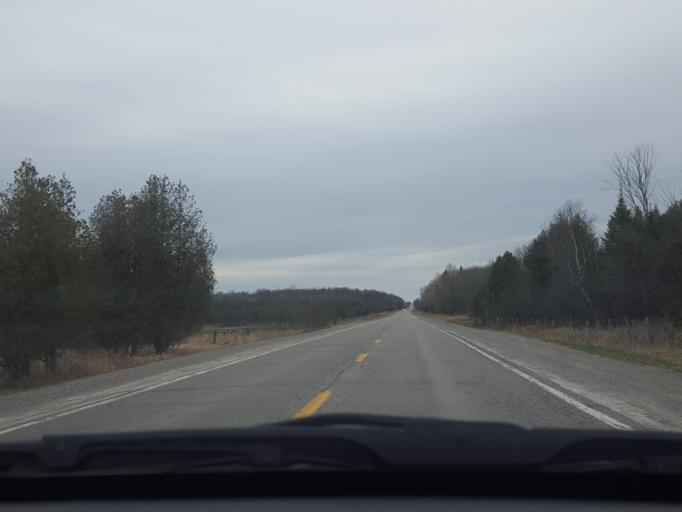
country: CA
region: Ontario
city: Uxbridge
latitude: 44.2868
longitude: -79.1665
